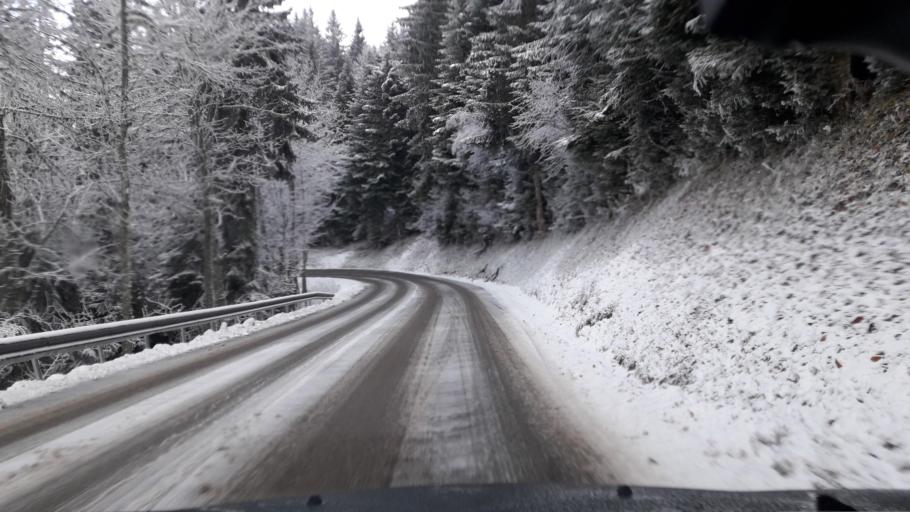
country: FR
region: Rhone-Alpes
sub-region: Departement de l'Isere
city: Allevard
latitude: 45.3930
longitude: 6.1028
